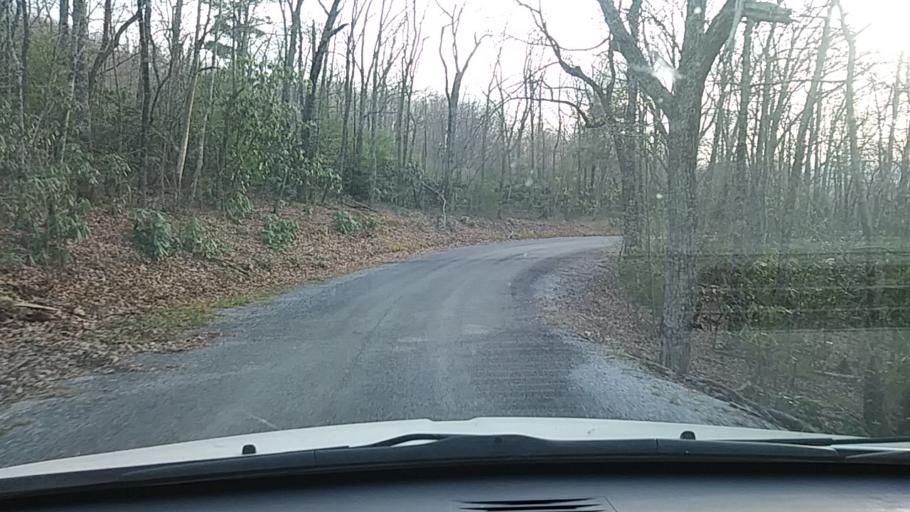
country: US
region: Tennessee
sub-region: Greene County
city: Tusculum
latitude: 36.0876
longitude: -82.6961
